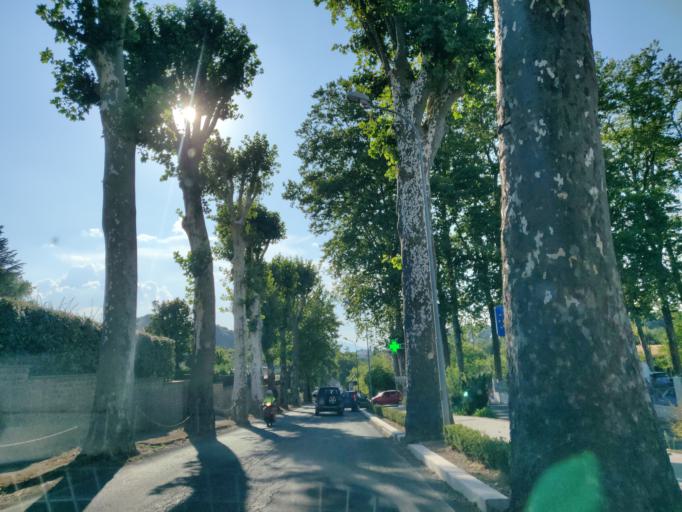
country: IT
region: Latium
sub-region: Provincia di Viterbo
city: Acquapendente
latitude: 42.7415
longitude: 11.8759
